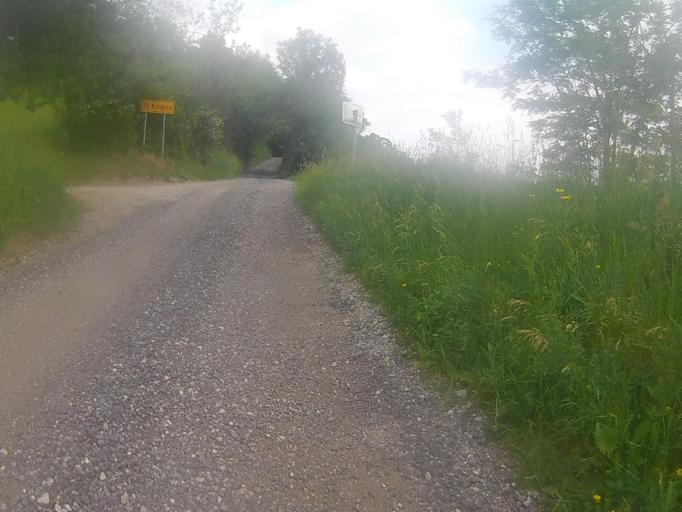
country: SI
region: Kungota
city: Zgornja Kungota
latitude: 46.6278
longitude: 15.5947
